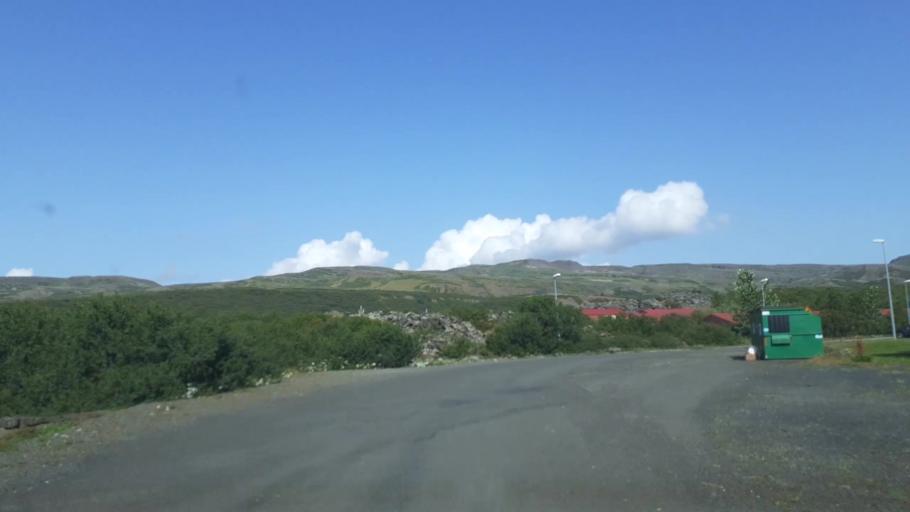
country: IS
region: West
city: Borgarnes
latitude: 64.7656
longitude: -21.5546
